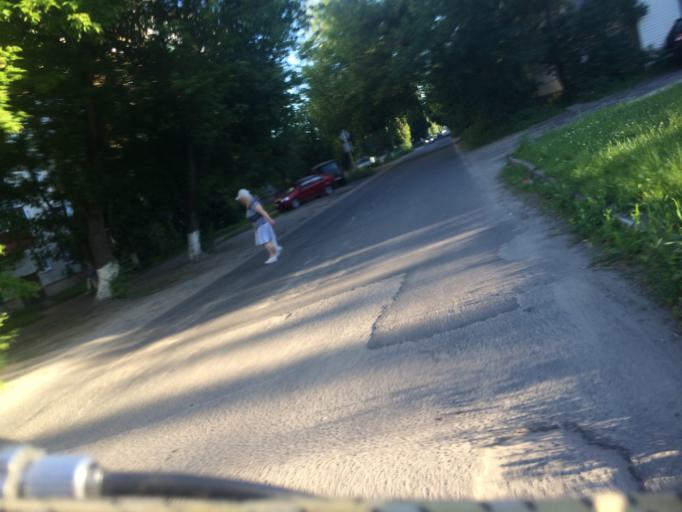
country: RU
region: Kursk
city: Kursk
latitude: 51.6739
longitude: 36.1547
